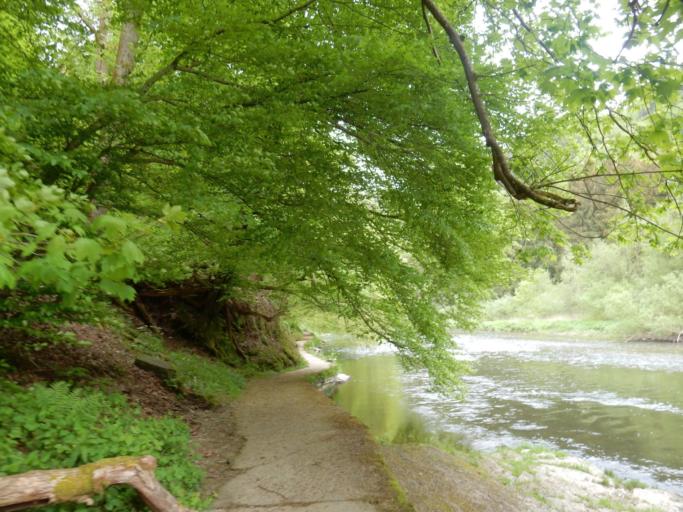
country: BE
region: Wallonia
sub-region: Province du Luxembourg
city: Bouillon
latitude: 49.7908
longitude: 5.0502
